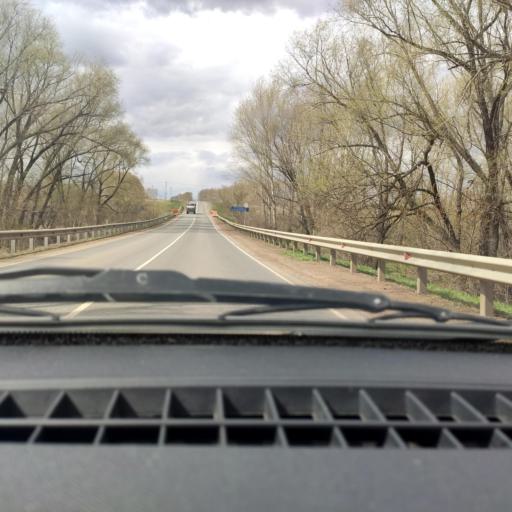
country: RU
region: Bashkortostan
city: Alekseyevka
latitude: 55.0530
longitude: 55.1247
